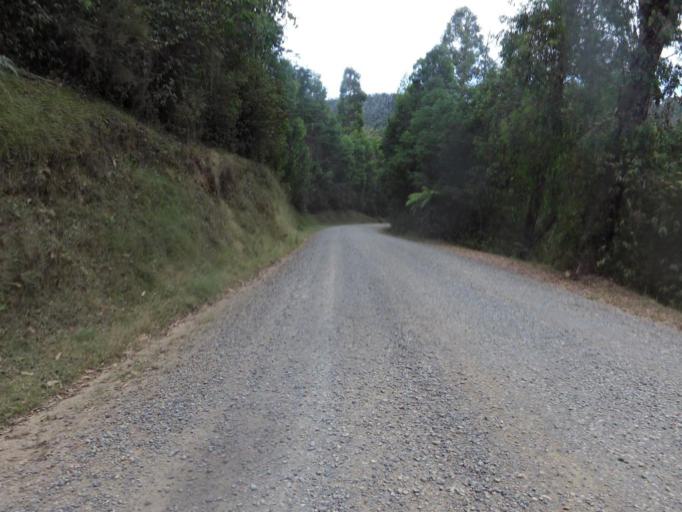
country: AU
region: Victoria
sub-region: Yarra Ranges
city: Healesville
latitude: -37.4026
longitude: 145.5592
